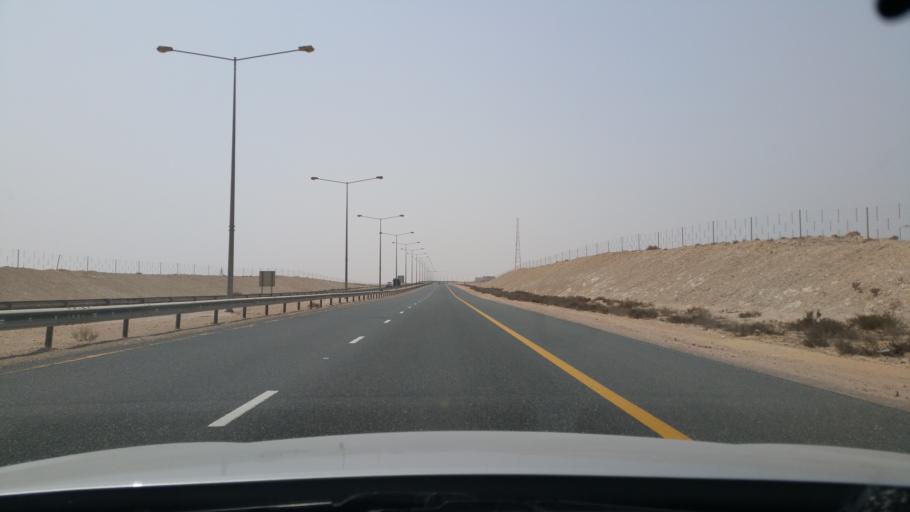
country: QA
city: Umm Bab
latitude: 25.3210
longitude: 50.7892
